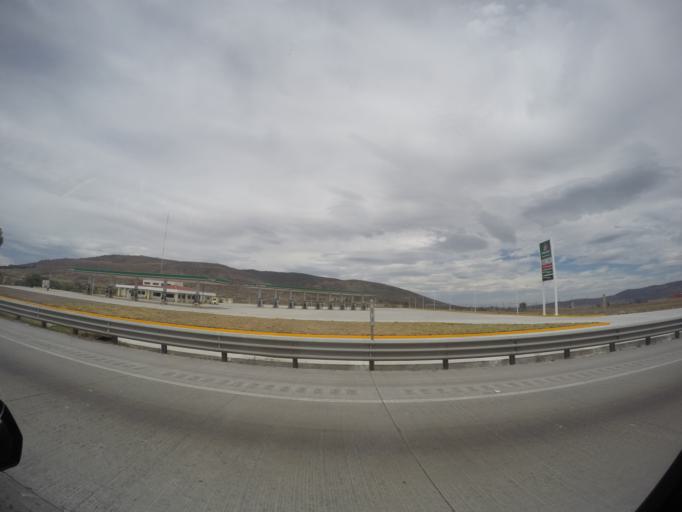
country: MX
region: Mexico
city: San Francisco Soyaniquilpan
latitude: 19.9945
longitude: -99.4767
